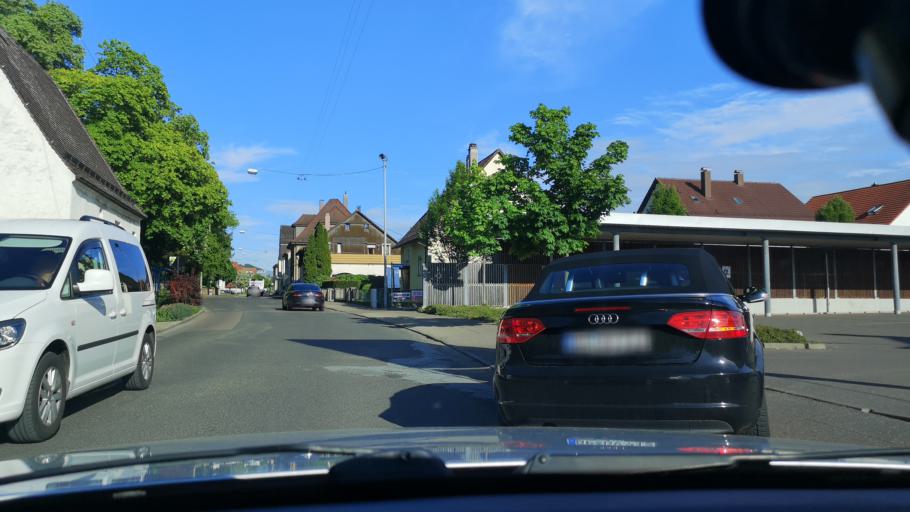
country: DE
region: Baden-Wuerttemberg
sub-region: Regierungsbezirk Stuttgart
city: Eislingen
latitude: 48.6975
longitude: 9.7112
